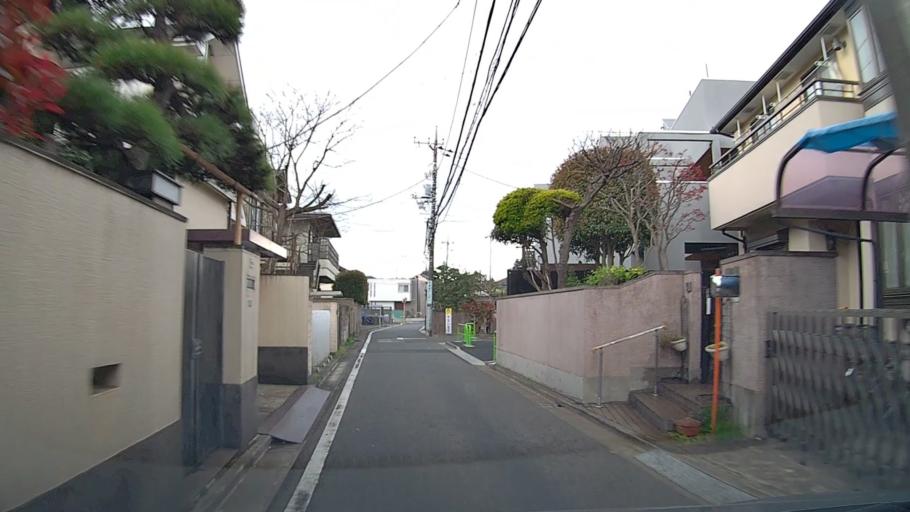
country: JP
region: Tokyo
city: Musashino
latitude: 35.7469
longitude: 139.5900
